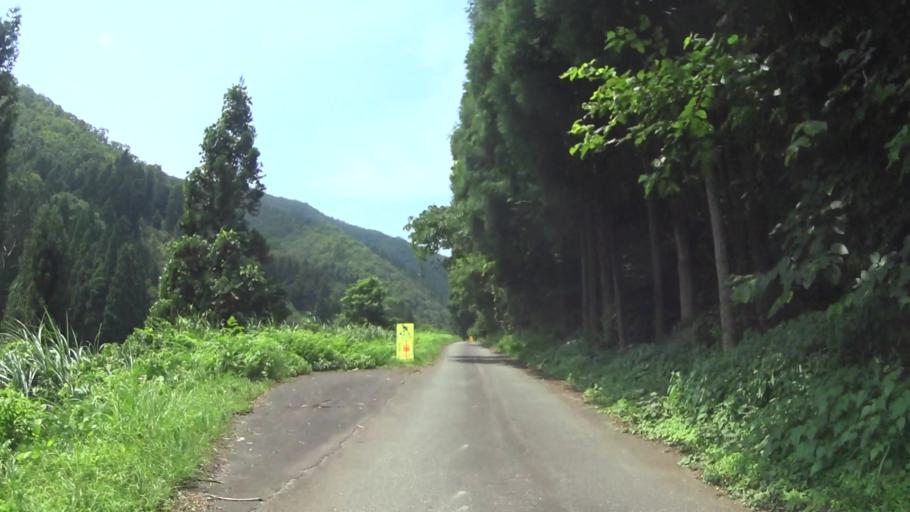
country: JP
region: Kyoto
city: Ayabe
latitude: 35.3009
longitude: 135.4077
